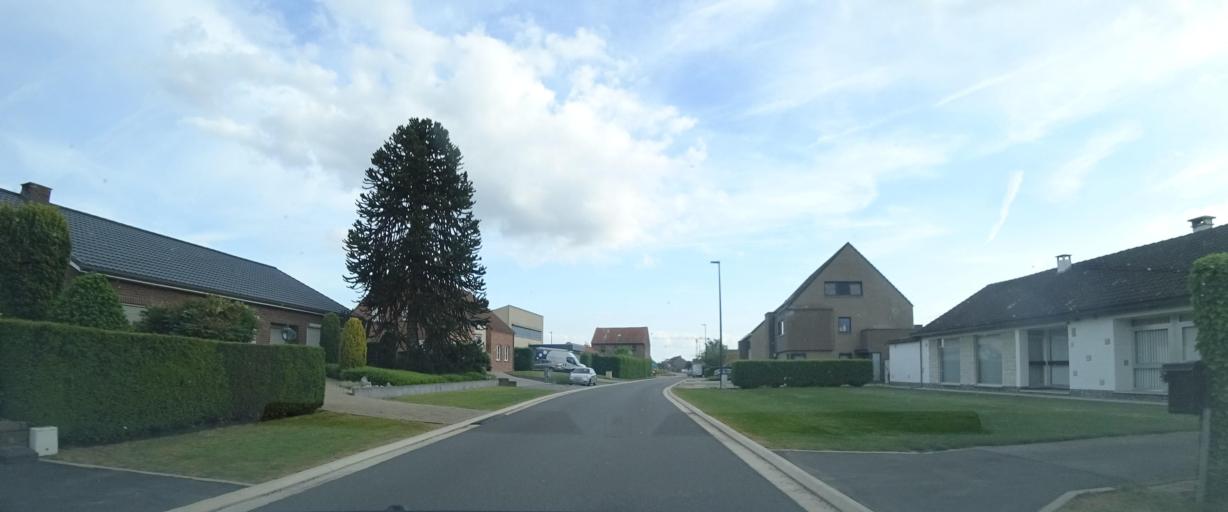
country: BE
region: Flanders
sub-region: Provincie Limburg
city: Nieuwerkerken
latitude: 50.8695
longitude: 5.1948
